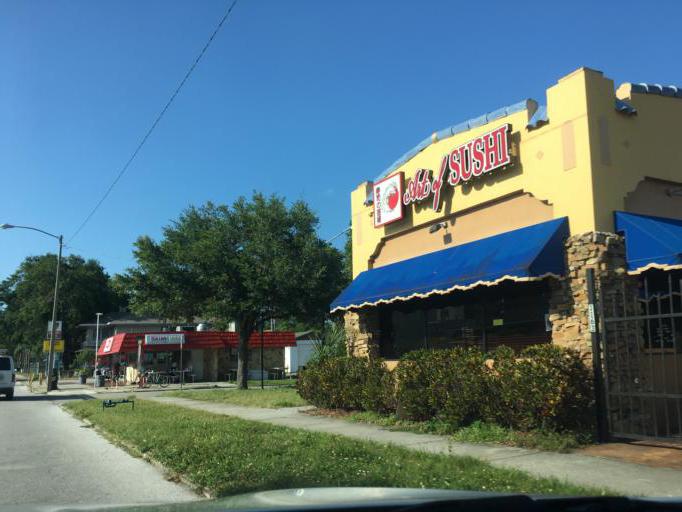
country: US
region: Florida
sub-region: Pinellas County
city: Saint Petersburg
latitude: 27.7836
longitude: -82.6467
